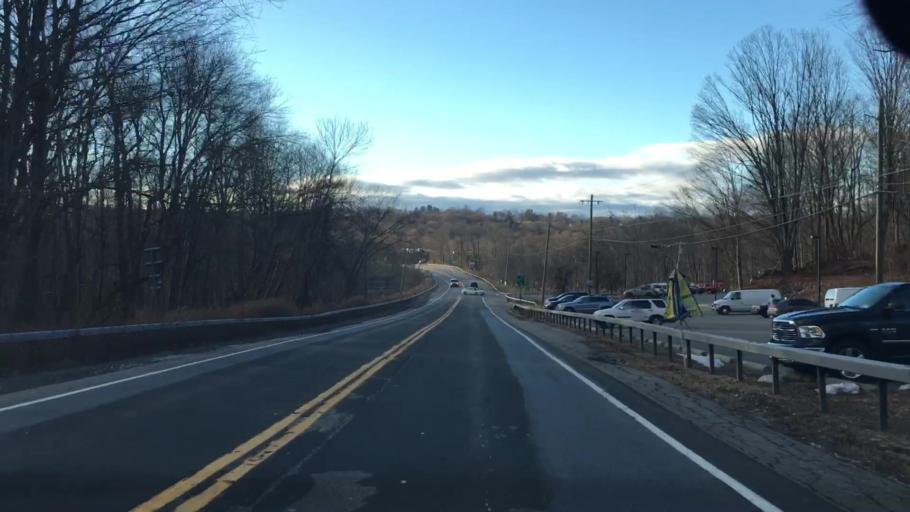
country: US
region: New York
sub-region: Putnam County
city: Lake Carmel
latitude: 41.4741
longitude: -73.6429
